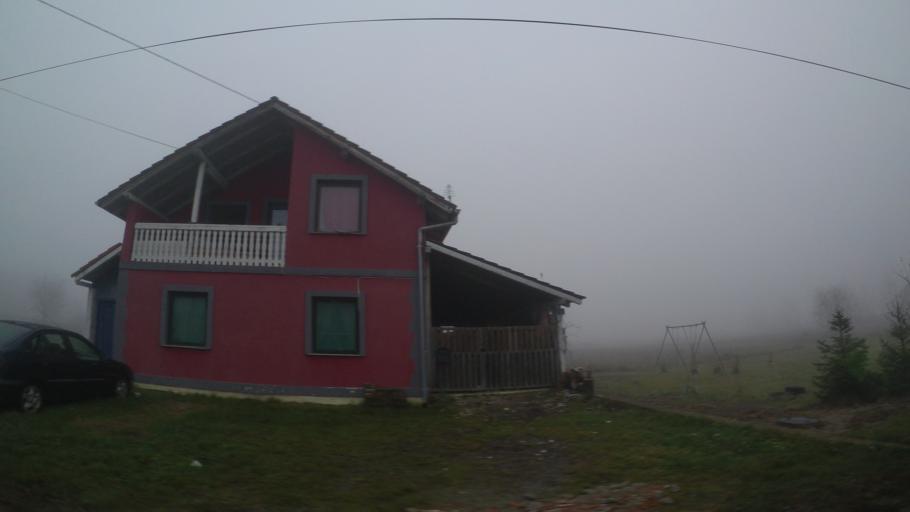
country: HR
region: Sisacko-Moslavacka
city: Glina
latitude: 45.3871
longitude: 16.1431
